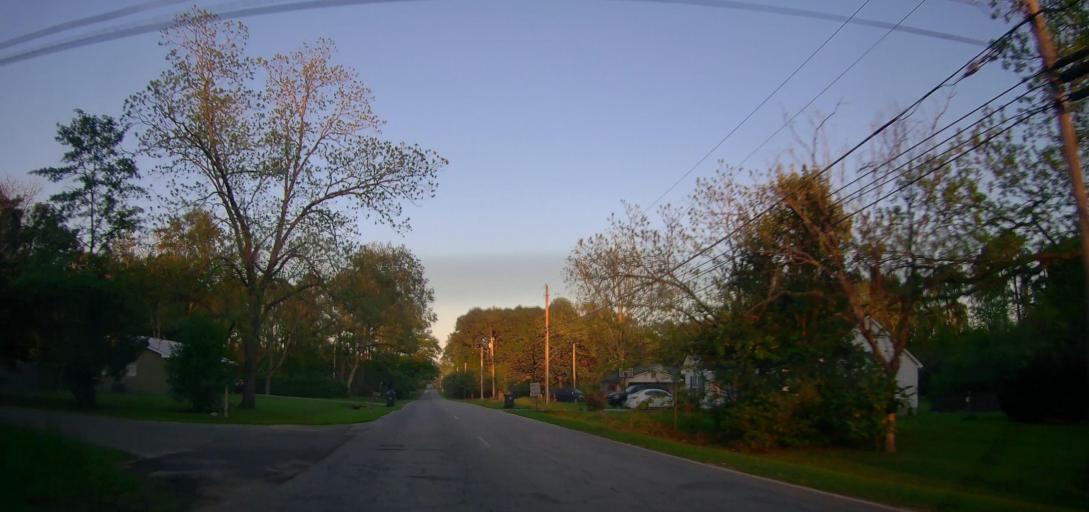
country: US
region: Georgia
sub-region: Ben Hill County
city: Fitzgerald
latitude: 31.7179
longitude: -83.2806
